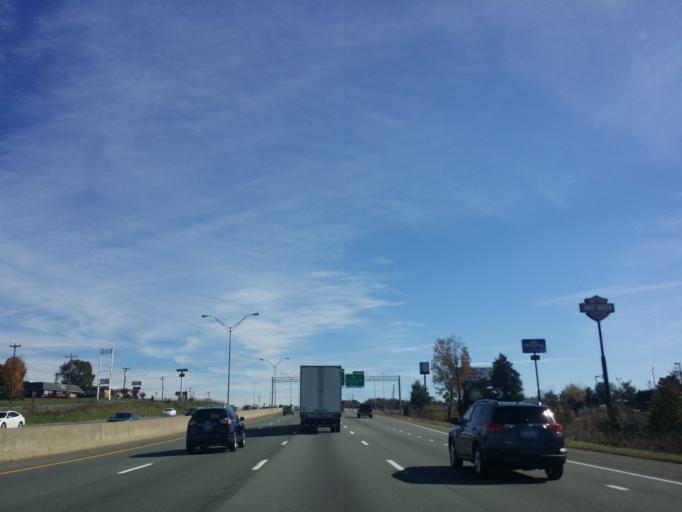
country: US
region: North Carolina
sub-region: Alamance County
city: Burlington
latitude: 36.0646
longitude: -79.4370
